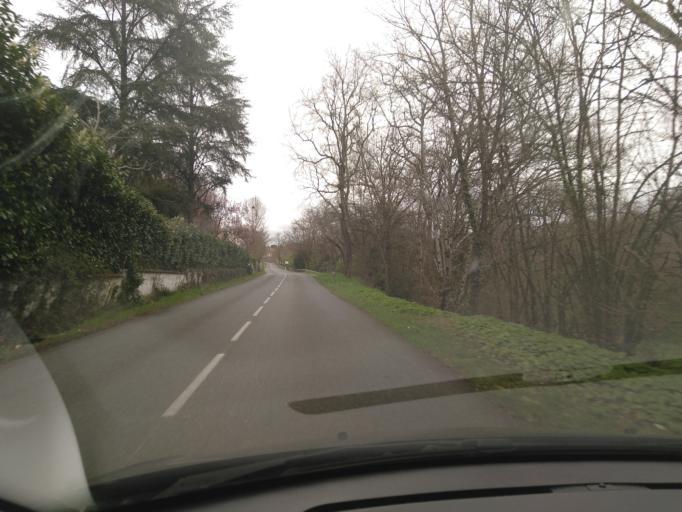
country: FR
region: Aquitaine
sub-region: Departement du Lot-et-Garonne
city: Foulayronnes
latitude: 44.2385
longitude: 0.6385
